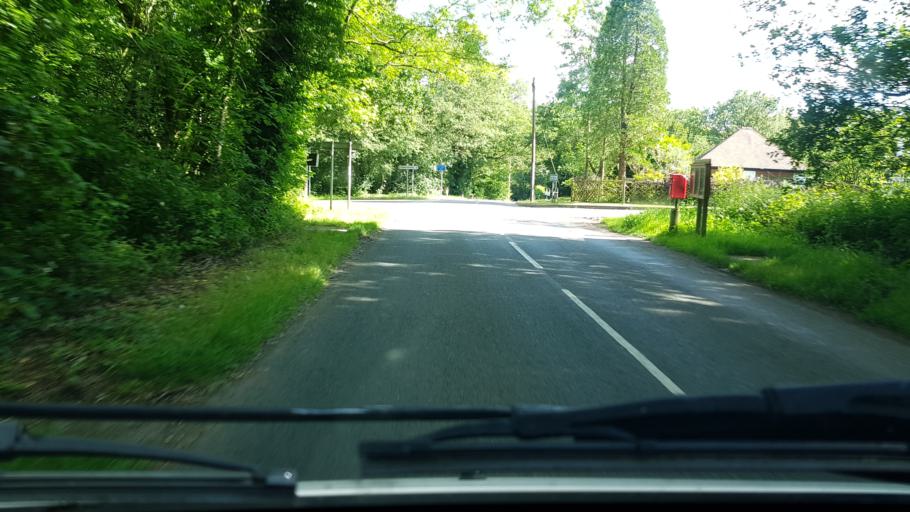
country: GB
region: England
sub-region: Worcestershire
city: Bewdley
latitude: 52.4005
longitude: -2.3044
